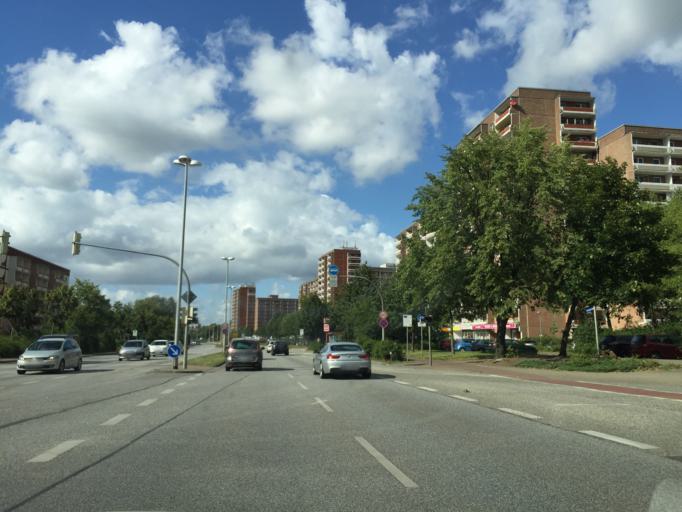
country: DE
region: Mecklenburg-Vorpommern
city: Neubrandenburg
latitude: 53.5415
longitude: 13.2654
